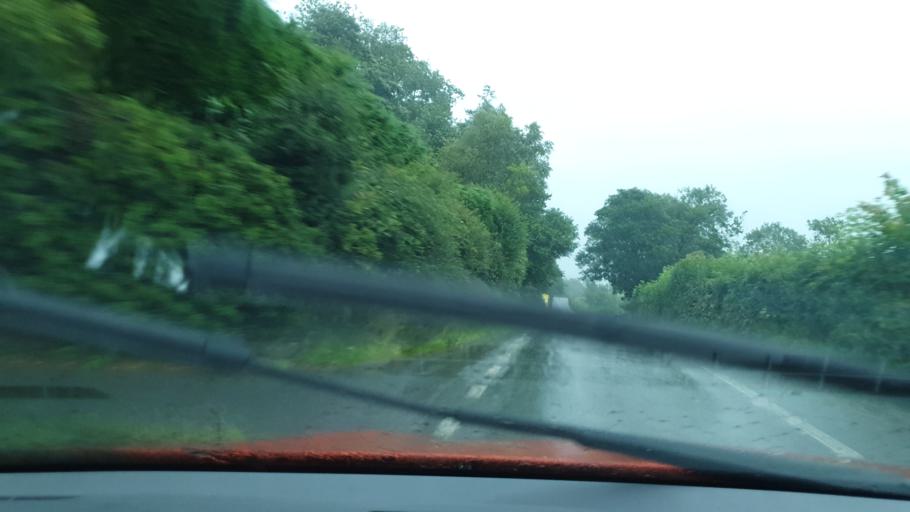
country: GB
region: England
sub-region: Cumbria
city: Askam in Furness
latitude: 54.2652
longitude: -3.1993
